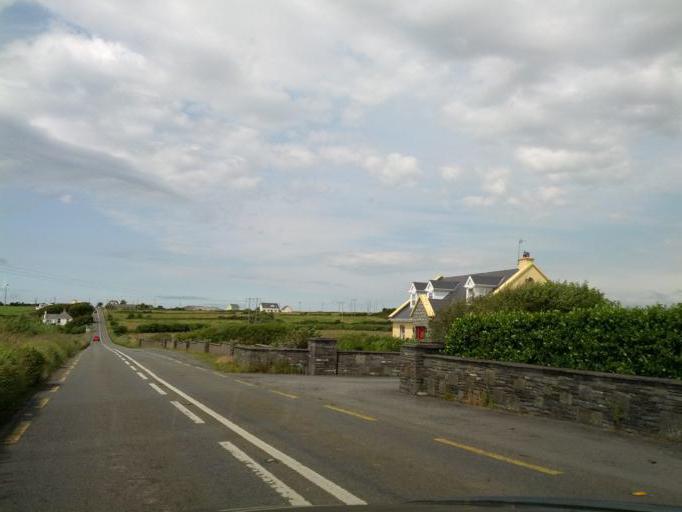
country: IE
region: Munster
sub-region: An Clar
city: Kilrush
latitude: 52.7902
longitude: -9.4421
